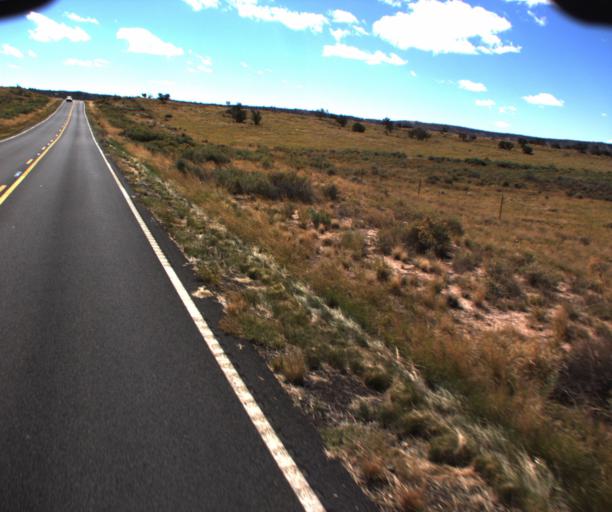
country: US
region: Arizona
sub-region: Apache County
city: Houck
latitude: 35.0525
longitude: -109.2753
